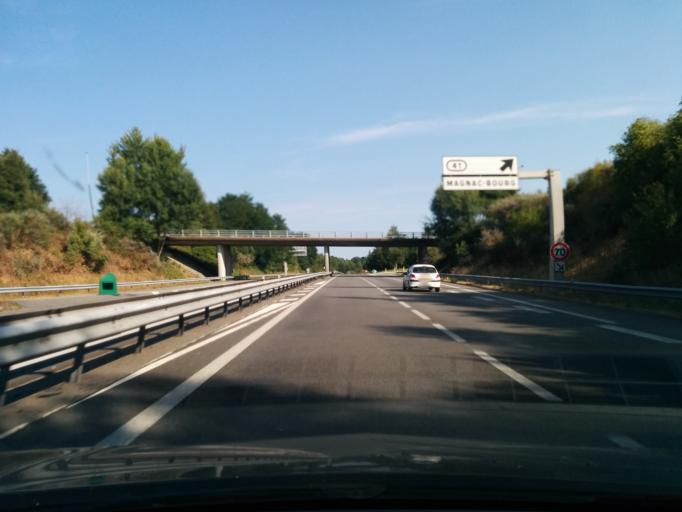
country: FR
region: Limousin
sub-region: Departement de la Haute-Vienne
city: Saint-Germain-les-Belles
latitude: 45.6262
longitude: 1.4398
